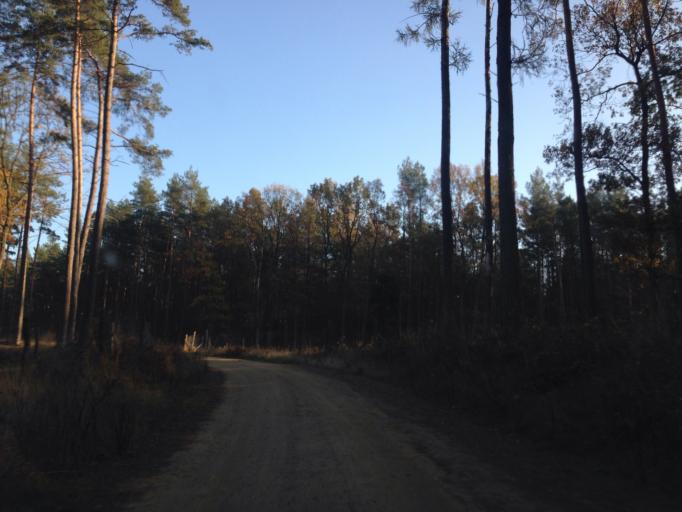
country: PL
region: Kujawsko-Pomorskie
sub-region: Powiat brodnicki
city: Gorzno
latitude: 53.1601
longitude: 19.6843
